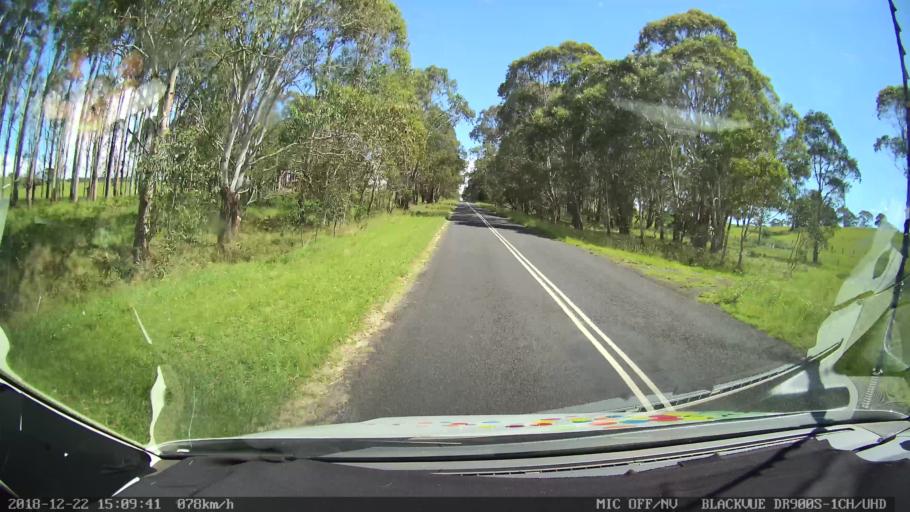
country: AU
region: New South Wales
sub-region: Bellingen
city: Dorrigo
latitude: -30.3264
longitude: 152.4066
